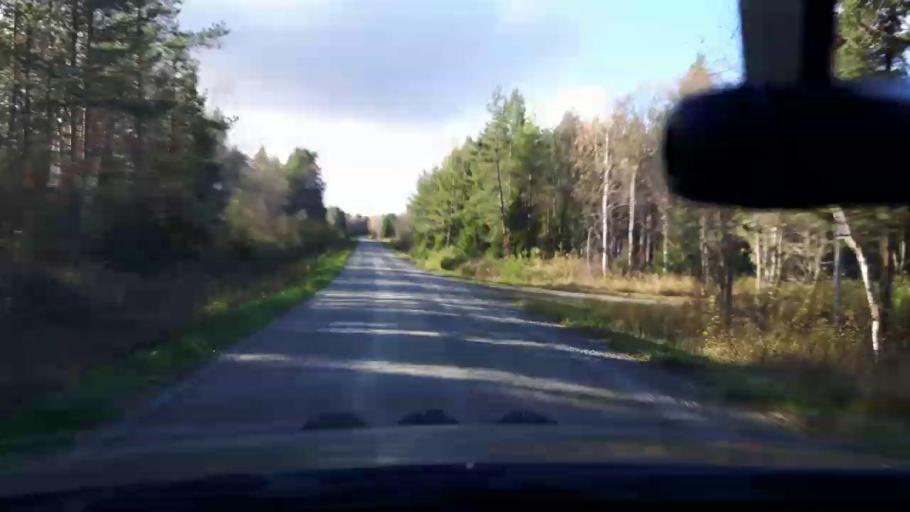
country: SE
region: Jaemtland
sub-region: Bergs Kommun
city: Hoverberg
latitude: 63.0264
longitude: 14.2807
